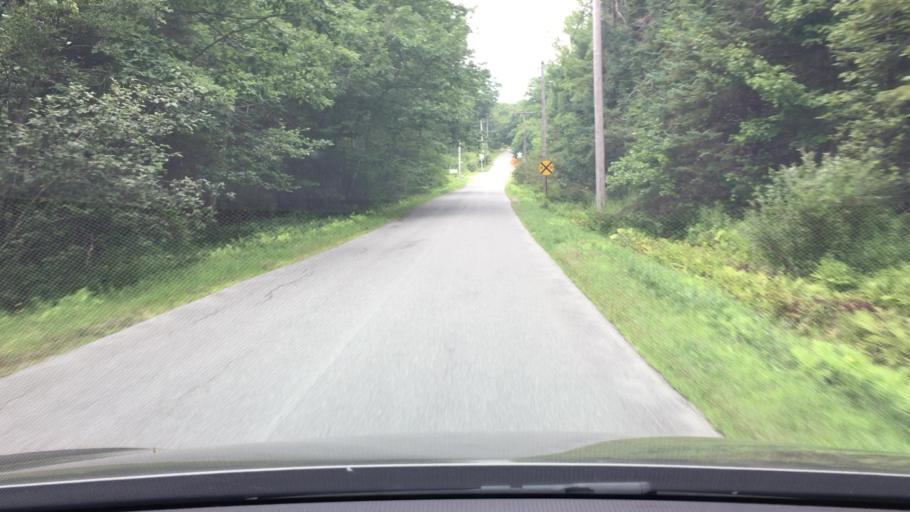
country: US
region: Maine
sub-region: Waldo County
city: Stockton Springs
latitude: 44.5070
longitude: -68.8126
